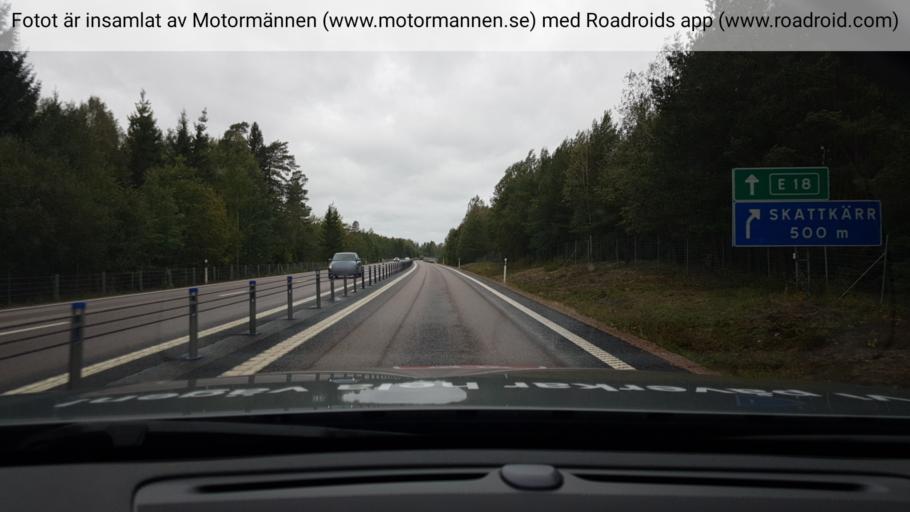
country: SE
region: Vaermland
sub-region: Karlstads Kommun
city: Skattkarr
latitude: 59.4178
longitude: 13.7296
